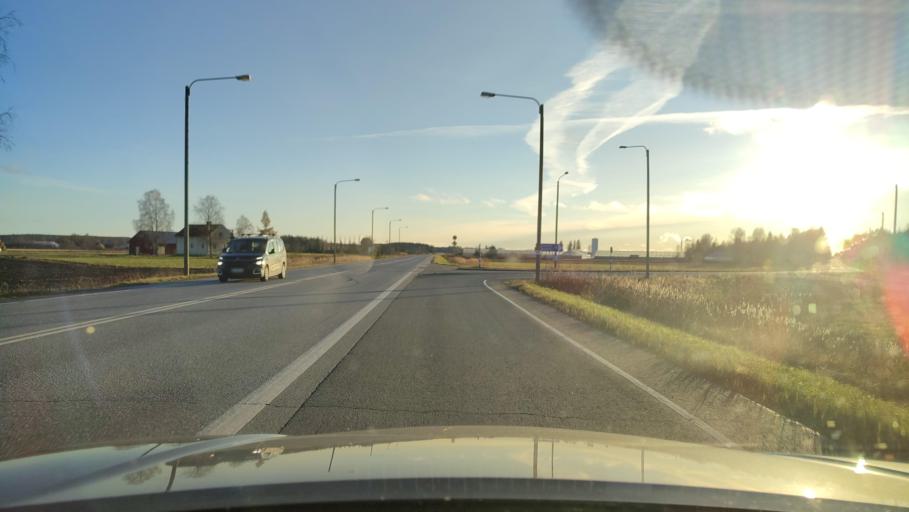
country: FI
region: Ostrobothnia
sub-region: Vaasa
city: Malax
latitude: 62.7090
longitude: 21.6080
